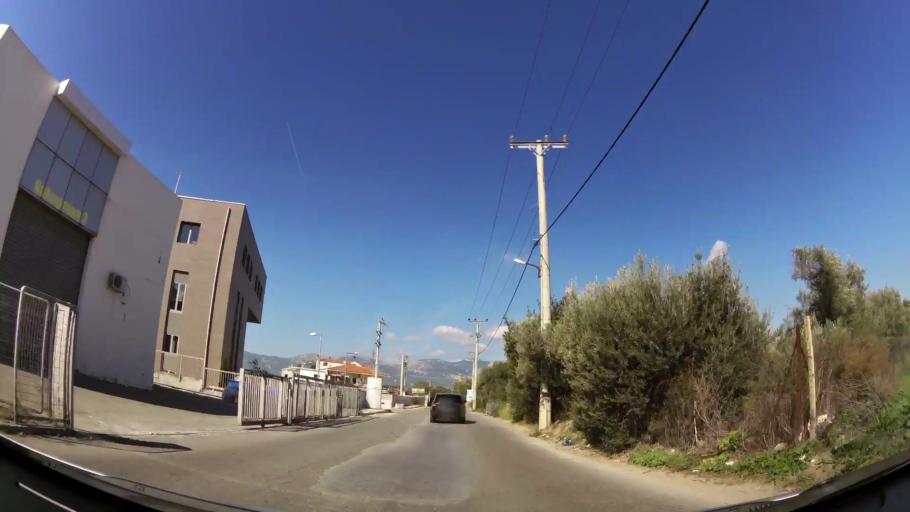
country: GR
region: Attica
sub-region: Nomarchia Athinas
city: Lykovrysi
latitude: 38.0789
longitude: 23.7938
